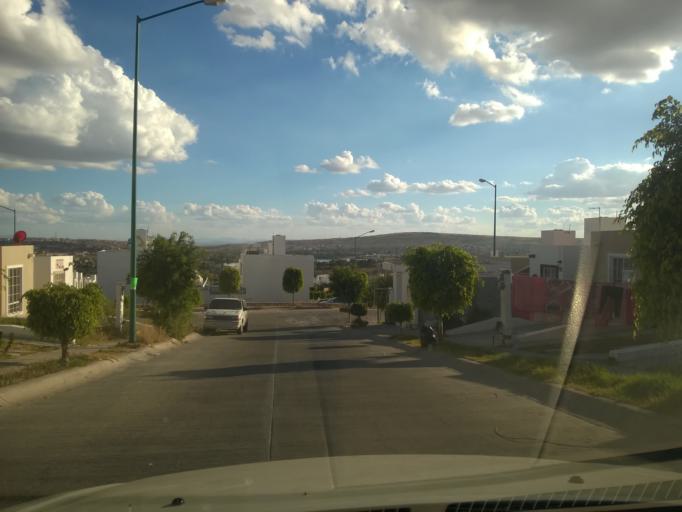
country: MX
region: Guanajuato
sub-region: Leon
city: La Ermita
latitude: 21.1586
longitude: -101.7412
